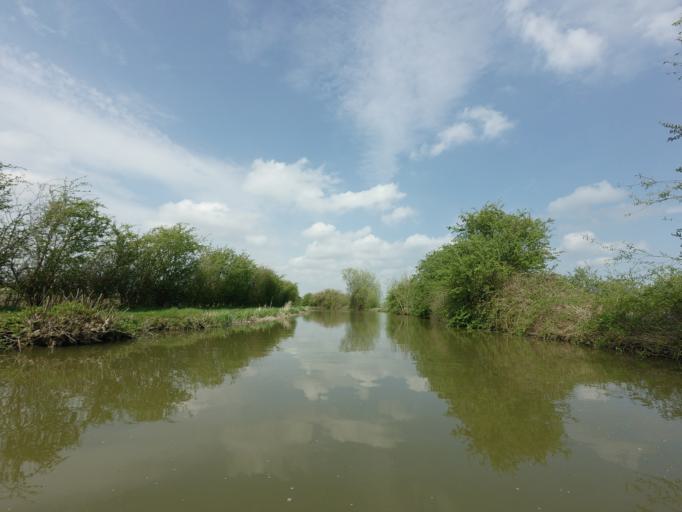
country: GB
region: England
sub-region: Central Bedfordshire
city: Leighton Buzzard
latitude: 51.8841
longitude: -0.6554
